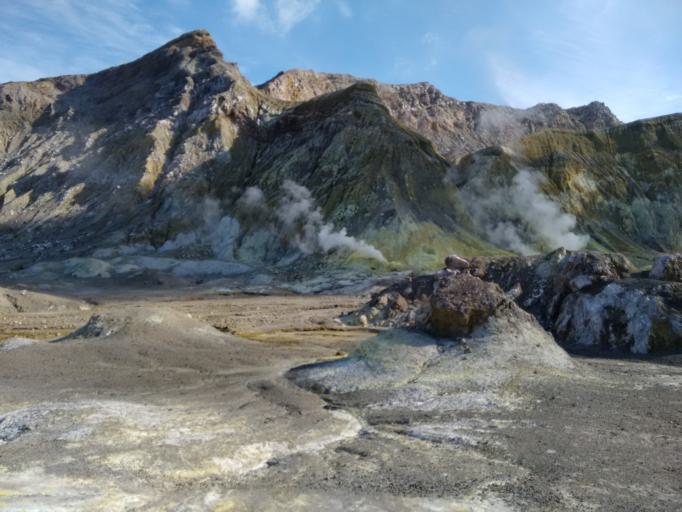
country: NZ
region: Bay of Plenty
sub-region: Whakatane District
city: Whakatane
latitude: -37.5230
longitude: 177.1895
